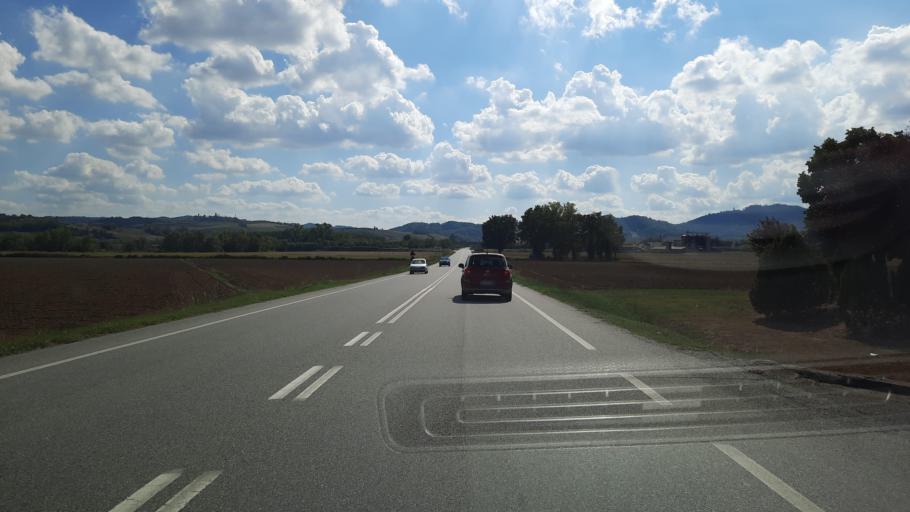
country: IT
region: Piedmont
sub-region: Provincia di Alessandria
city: Pontestura
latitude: 45.1188
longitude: 8.3261
